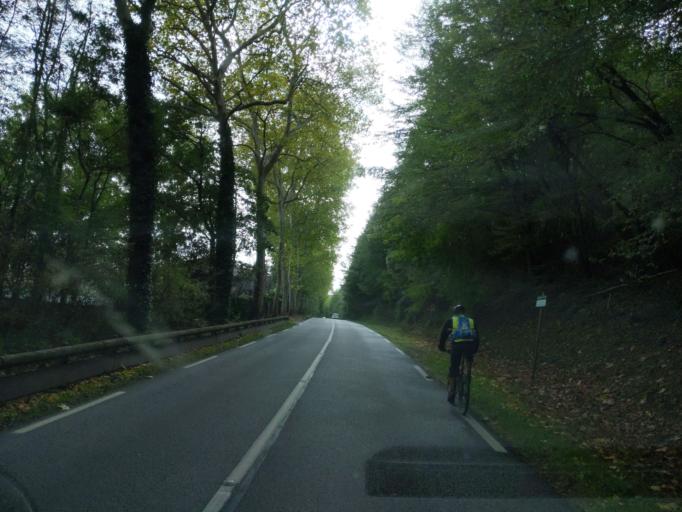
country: FR
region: Ile-de-France
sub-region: Departement des Yvelines
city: Chevreuse
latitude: 48.6950
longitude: 2.0187
